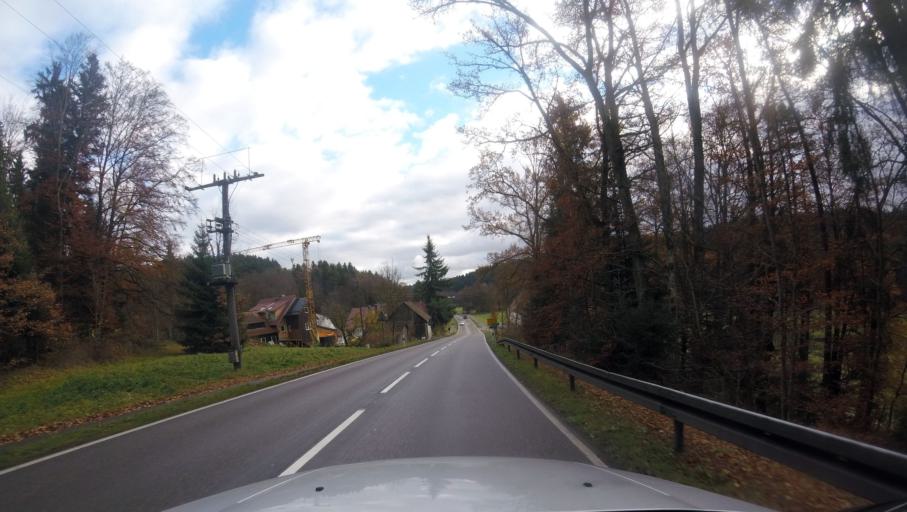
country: DE
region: Baden-Wuerttemberg
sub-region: Regierungsbezirk Stuttgart
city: Spraitbach
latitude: 48.8572
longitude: 9.7652
